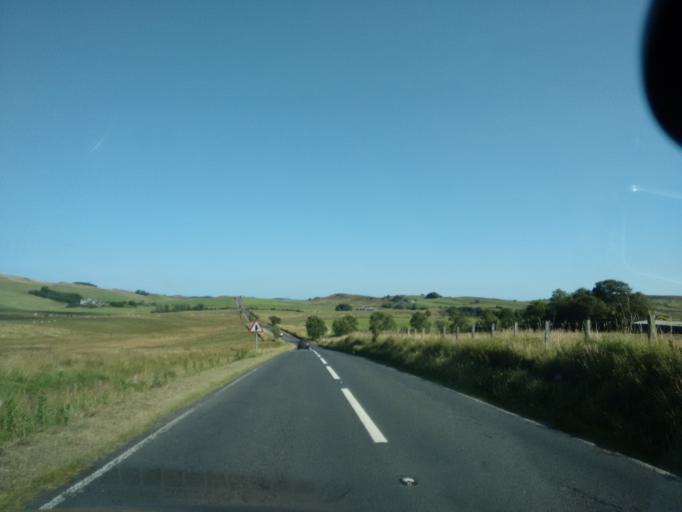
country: GB
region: England
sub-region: Northumberland
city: Bardon Mill
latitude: 54.9997
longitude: -2.3658
